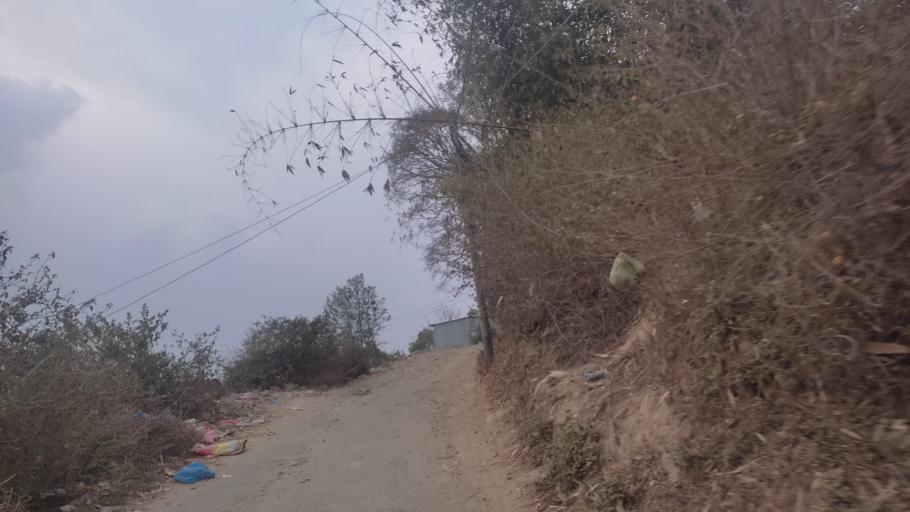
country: NP
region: Central Region
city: Kirtipur
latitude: 27.6648
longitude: 85.2866
